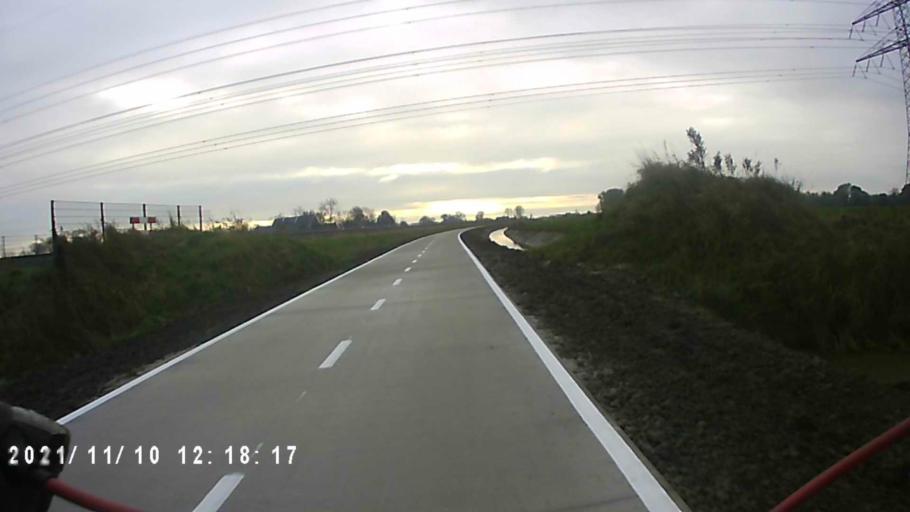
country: NL
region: Groningen
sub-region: Gemeente Winsum
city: Winsum
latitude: 53.3006
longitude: 6.5395
